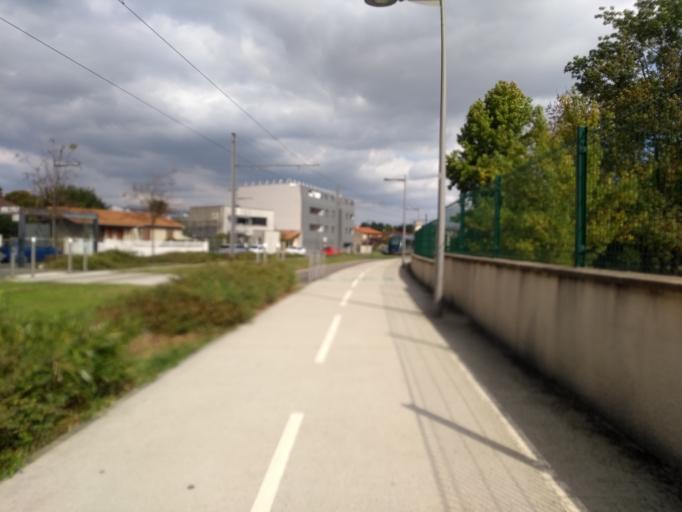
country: FR
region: Aquitaine
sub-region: Departement de la Gironde
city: Begles
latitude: 44.7957
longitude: -0.5577
